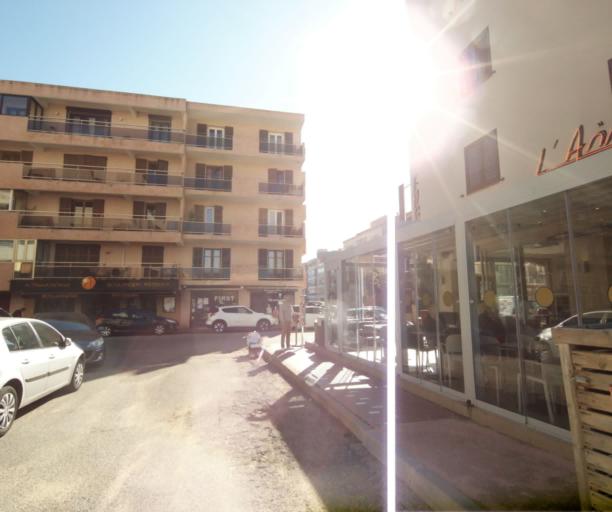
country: FR
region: Corsica
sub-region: Departement de la Corse-du-Sud
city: Propriano
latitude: 41.6749
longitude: 8.9003
